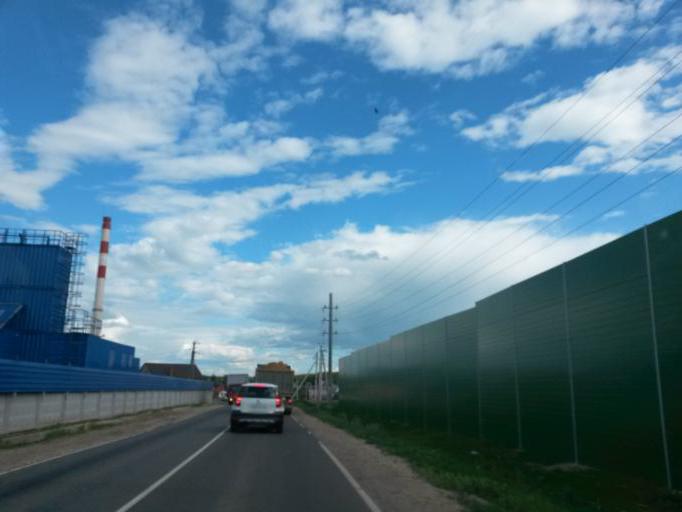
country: RU
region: Moskovskaya
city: Klimovsk
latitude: 55.3402
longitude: 37.5998
